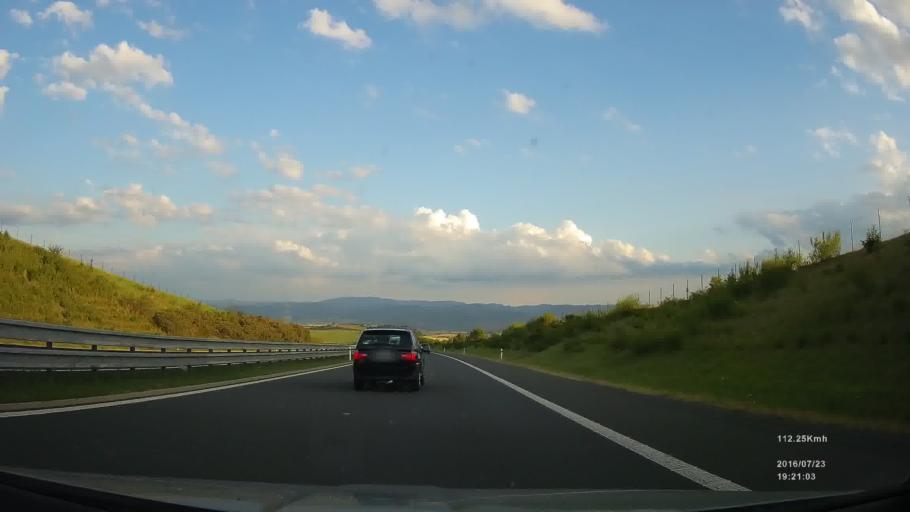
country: SK
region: Presovsky
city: Lubica
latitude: 49.0274
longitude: 20.4359
